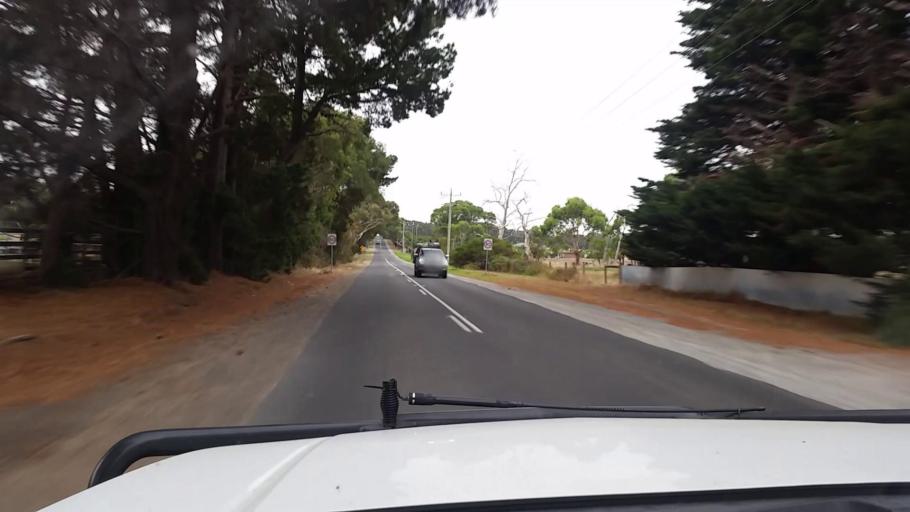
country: AU
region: Victoria
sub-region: Mornington Peninsula
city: Balnarring
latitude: -38.3346
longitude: 145.1457
